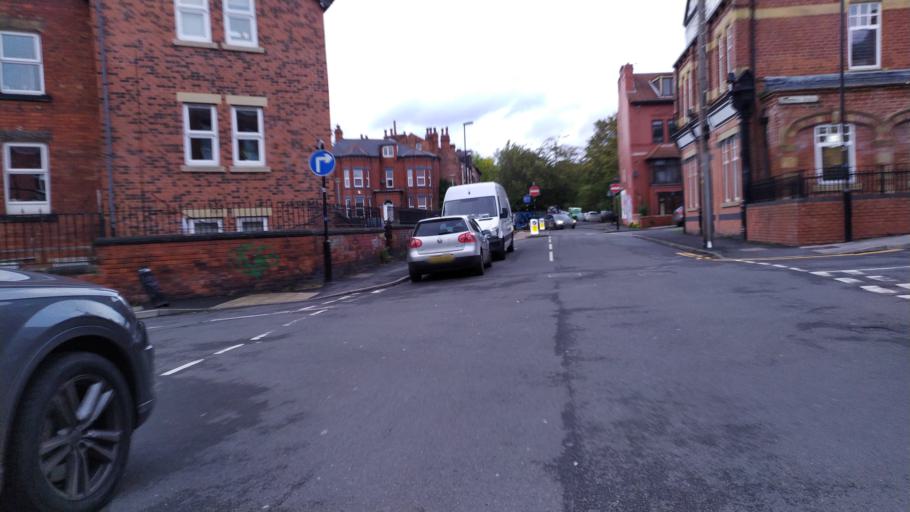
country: GB
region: England
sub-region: City and Borough of Leeds
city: Leeds
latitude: 53.8122
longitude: -1.5674
